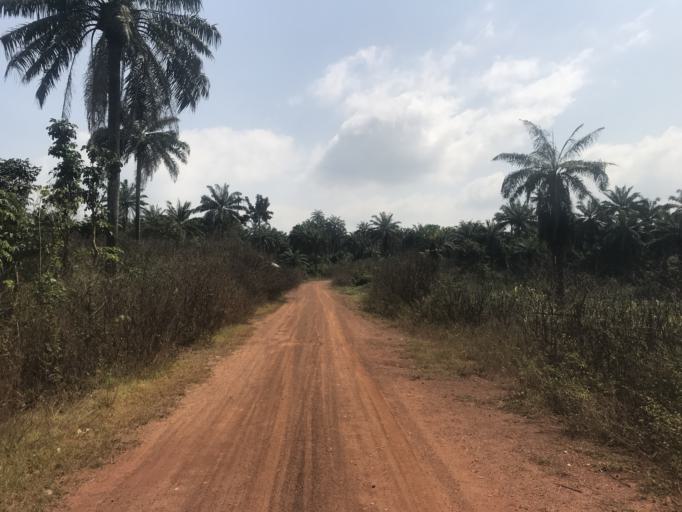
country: NG
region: Osun
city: Ikirun
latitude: 7.8329
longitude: 4.6351
